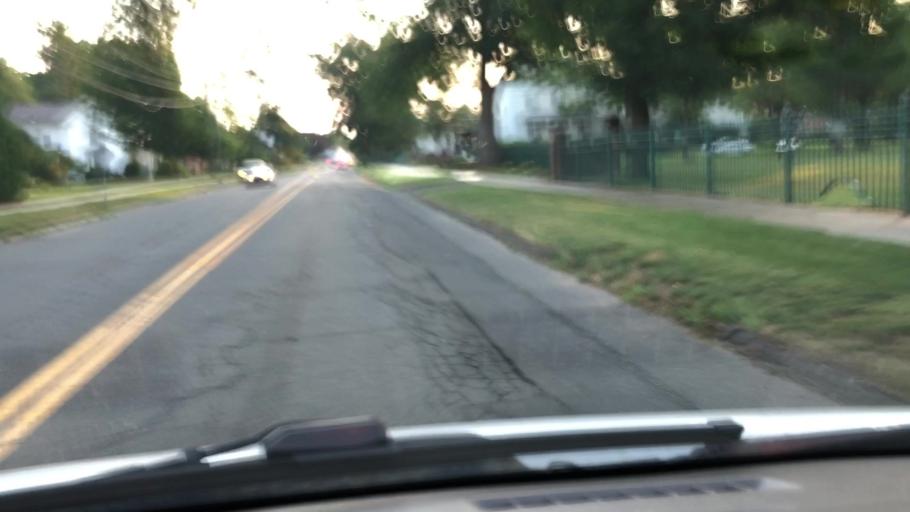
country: US
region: Massachusetts
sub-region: Hampshire County
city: Easthampton
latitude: 42.2657
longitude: -72.6754
